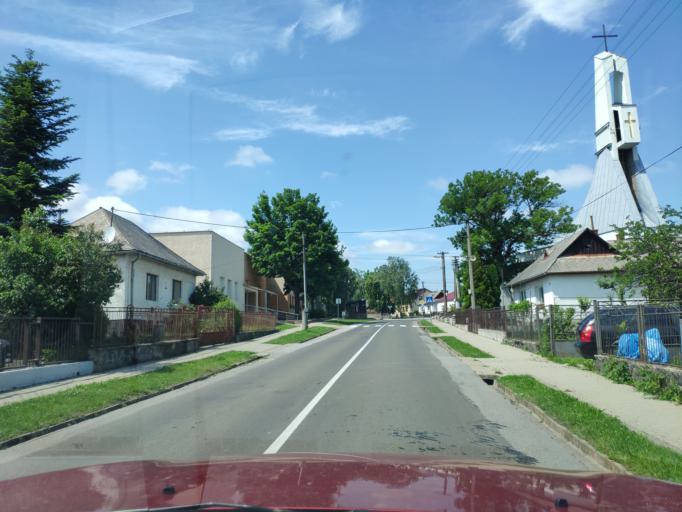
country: SK
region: Kosicky
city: Secovce
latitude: 48.7584
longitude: 21.6421
